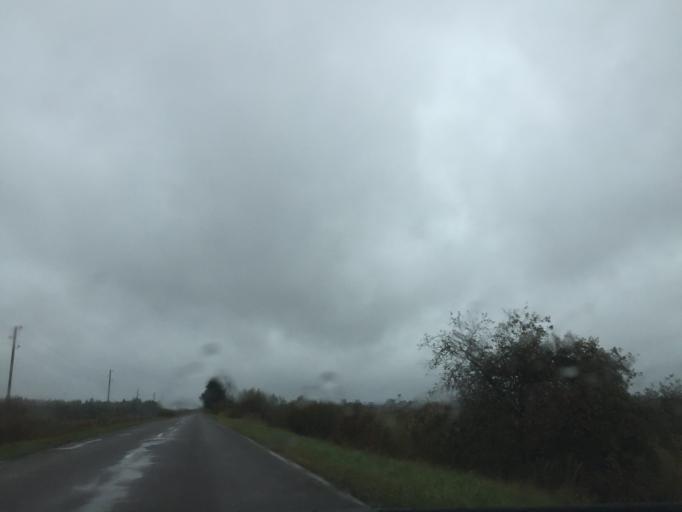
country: LV
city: Tireli
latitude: 56.8177
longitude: 23.5708
